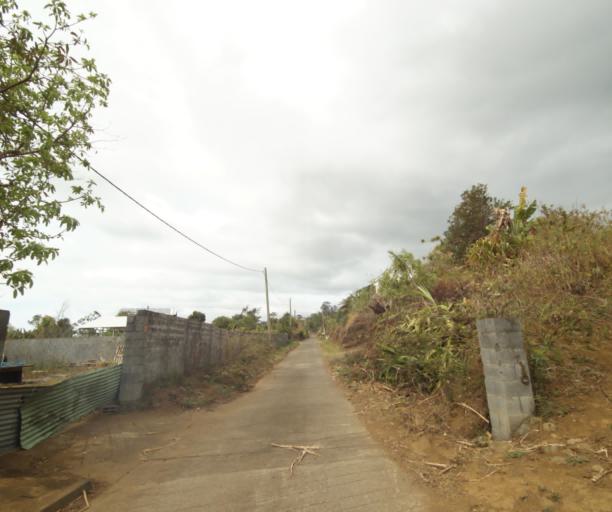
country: RE
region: Reunion
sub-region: Reunion
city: Saint-Paul
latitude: -21.0182
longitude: 55.3272
